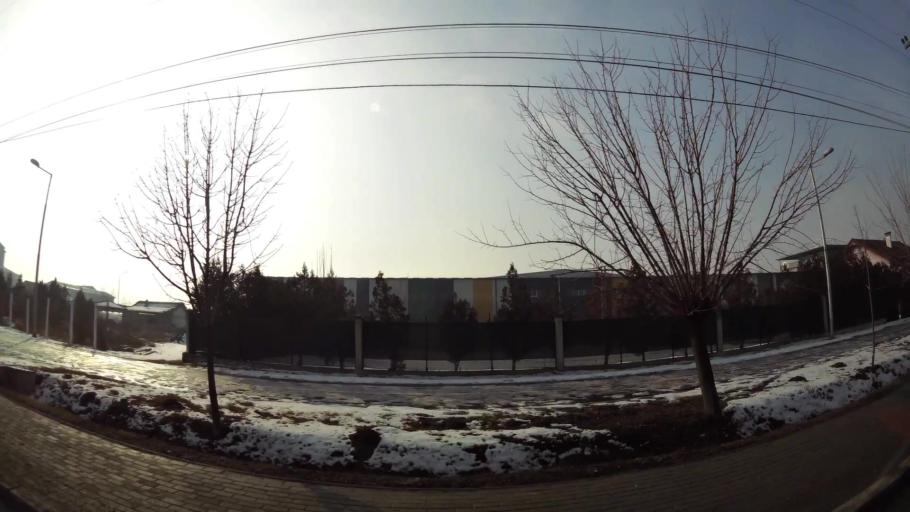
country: MK
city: Kadino
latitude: 41.9758
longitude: 21.5943
